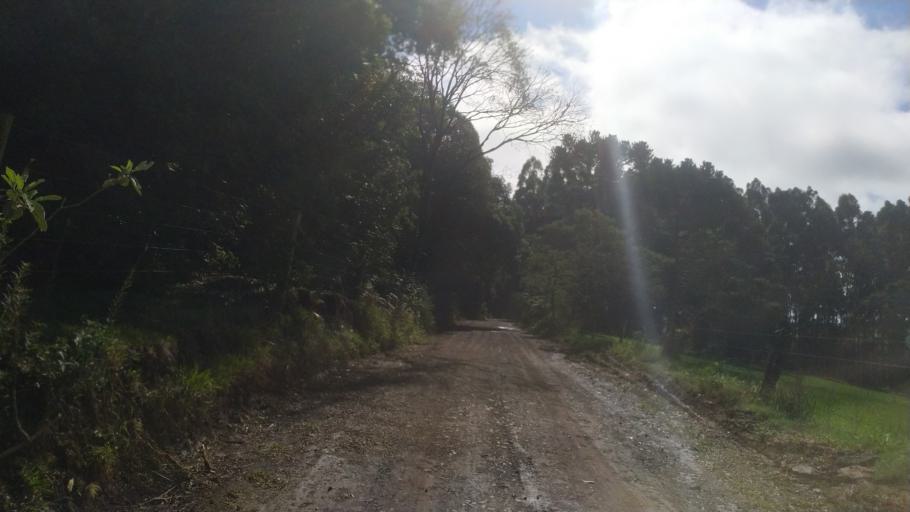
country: BR
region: Santa Catarina
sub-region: Chapeco
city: Chapeco
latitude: -27.1615
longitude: -52.5972
